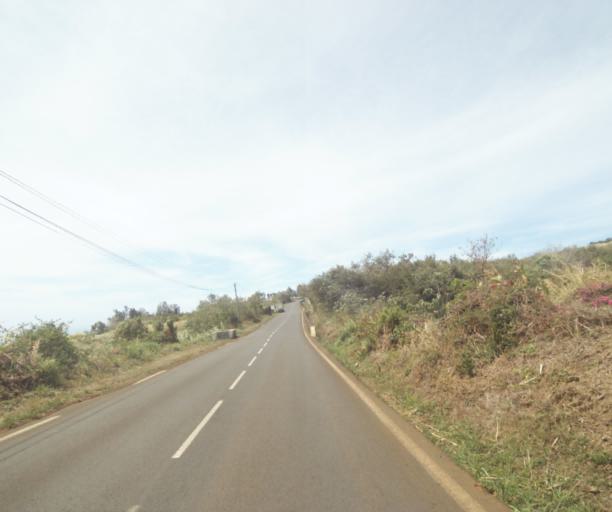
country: RE
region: Reunion
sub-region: Reunion
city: Saint-Paul
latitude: -21.0411
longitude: 55.2878
